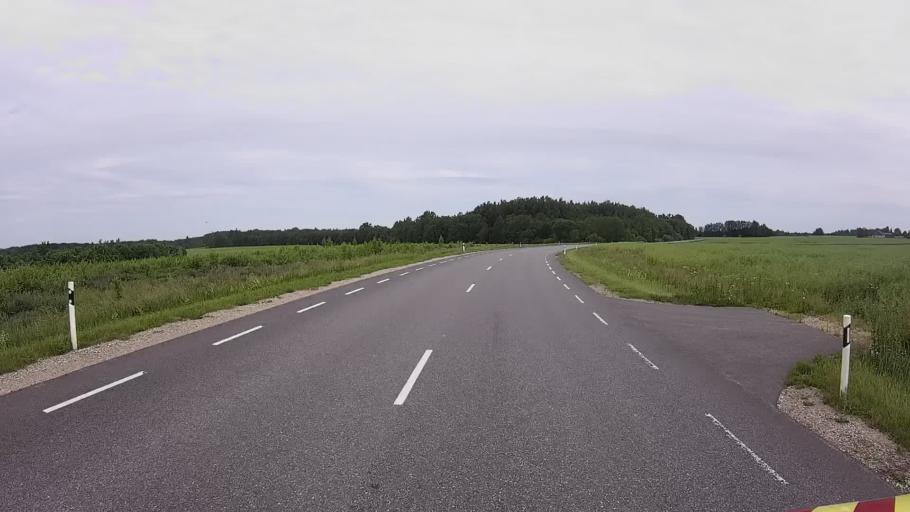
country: EE
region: Viljandimaa
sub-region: Karksi vald
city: Karksi-Nuia
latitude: 58.1688
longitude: 25.5805
